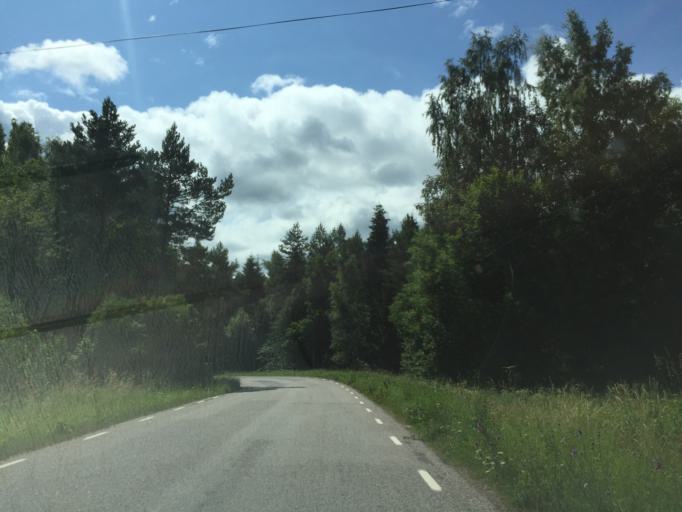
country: SE
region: OEstergoetland
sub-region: Odeshogs Kommun
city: OEdeshoeg
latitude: 58.1838
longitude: 14.7227
